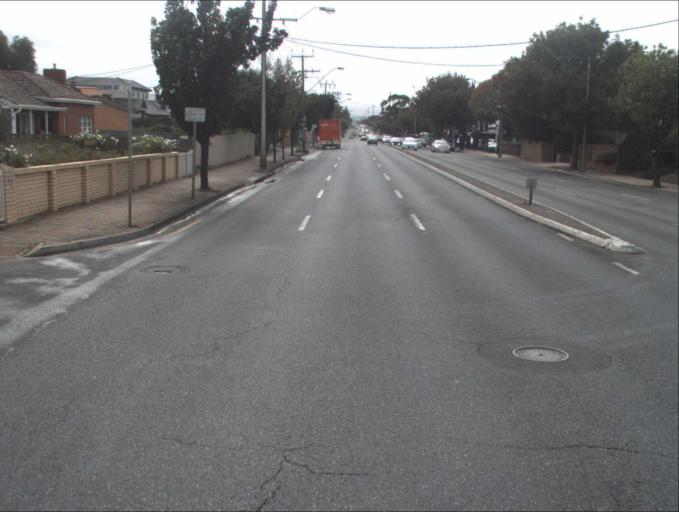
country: AU
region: South Australia
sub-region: Port Adelaide Enfield
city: Klemzig
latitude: -34.8858
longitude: 138.6179
